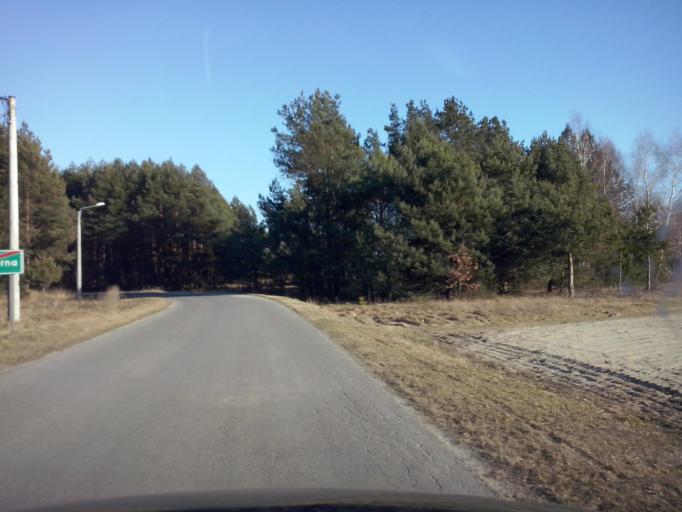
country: PL
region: Subcarpathian Voivodeship
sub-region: Powiat nizanski
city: Harasiuki
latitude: 50.5344
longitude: 22.4766
